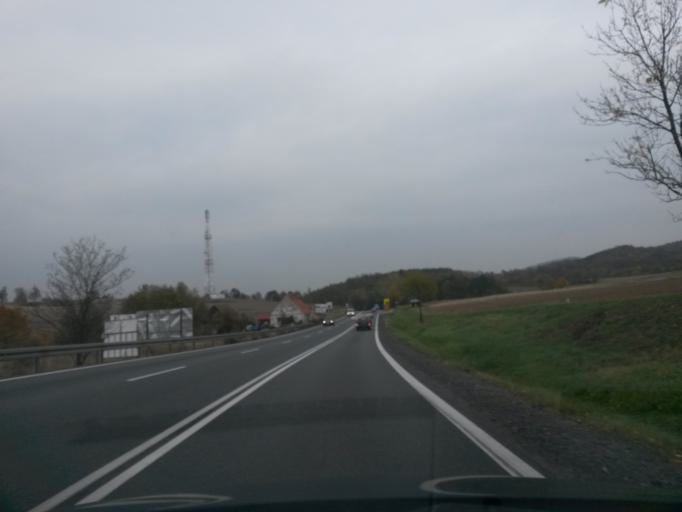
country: PL
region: Lower Silesian Voivodeship
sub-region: Powiat zabkowicki
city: Bardo
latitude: 50.4776
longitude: 16.7072
